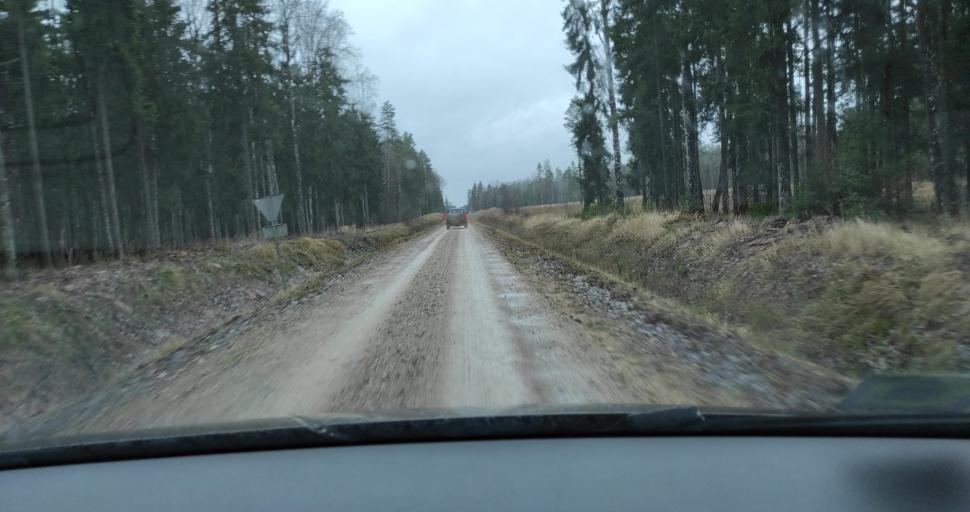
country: LV
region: Skrunda
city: Skrunda
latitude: 56.5560
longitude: 22.0817
